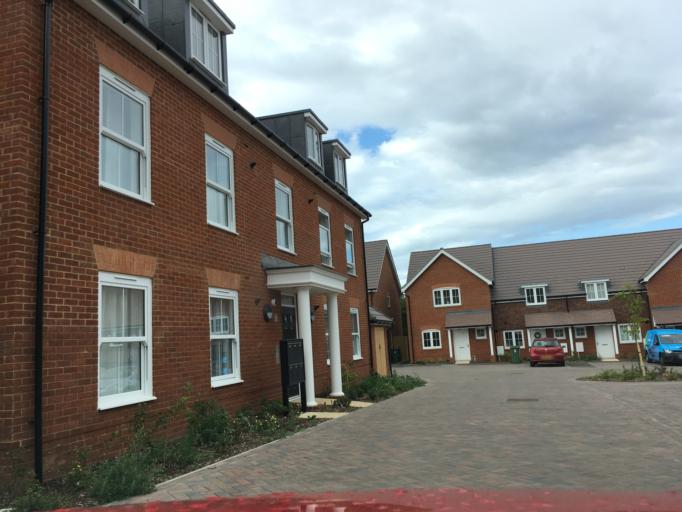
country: GB
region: England
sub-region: Kent
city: Maidstone
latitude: 51.2377
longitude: 0.4968
